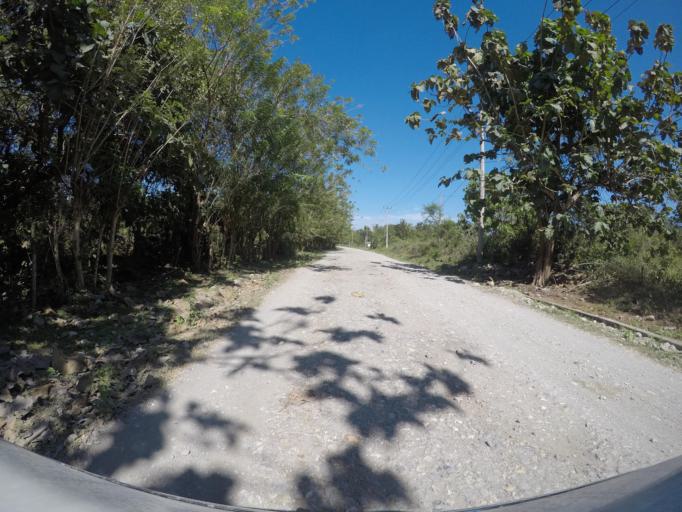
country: TL
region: Viqueque
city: Viqueque
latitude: -8.9719
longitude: 126.0572
